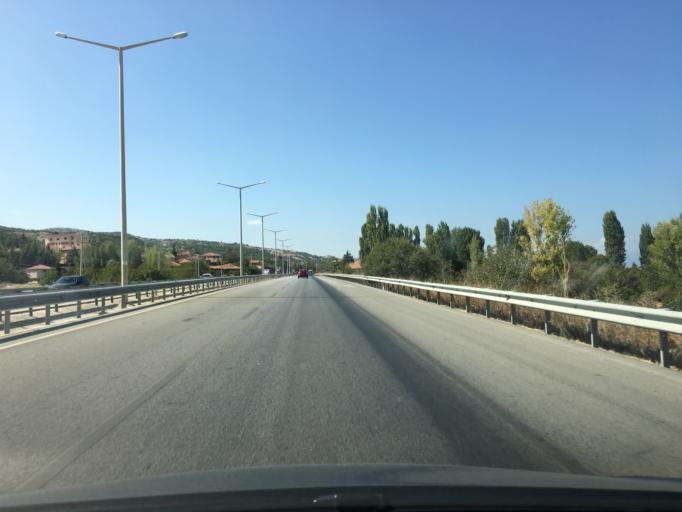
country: TR
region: Burdur
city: Burdur
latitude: 37.7610
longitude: 30.3452
